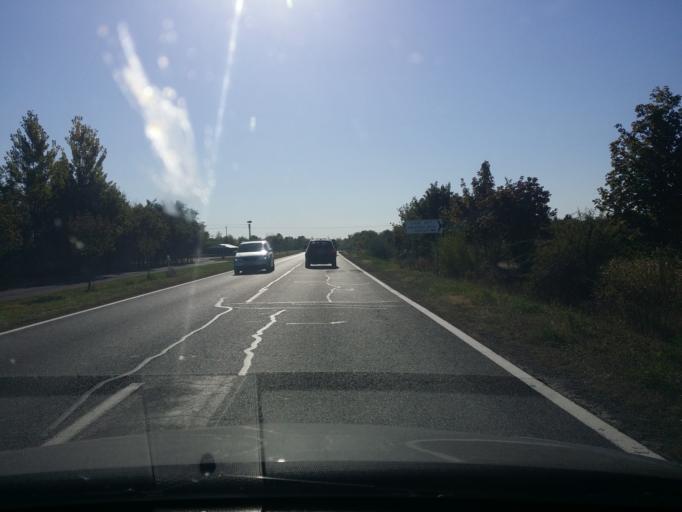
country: HU
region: Bekes
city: Bekescsaba
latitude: 46.6987
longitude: 21.1177
